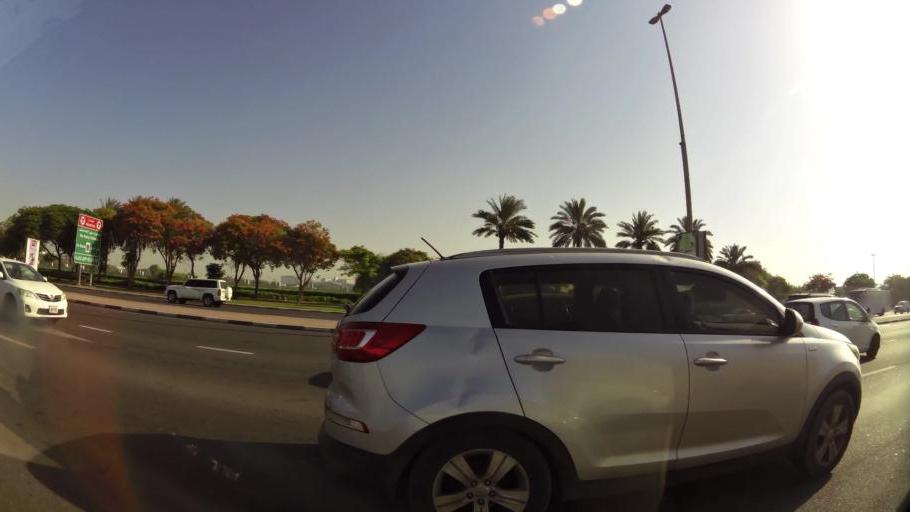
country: AE
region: Ash Shariqah
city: Sharjah
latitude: 25.2678
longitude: 55.3589
